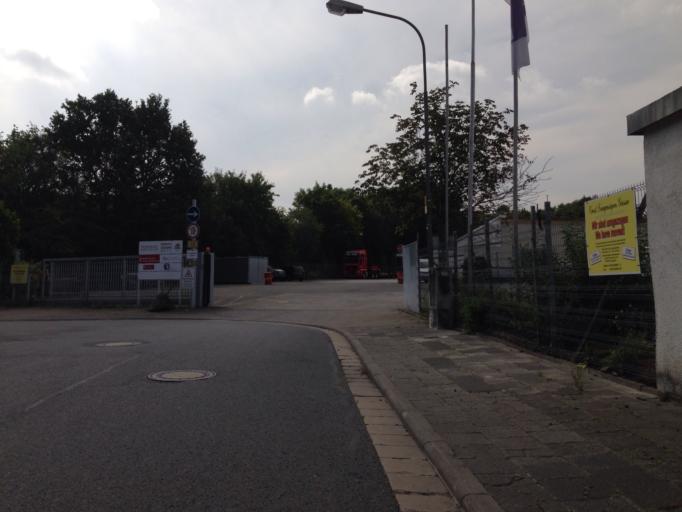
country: DE
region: Hesse
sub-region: Regierungsbezirk Giessen
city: Giessen
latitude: 50.5949
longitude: 8.7101
